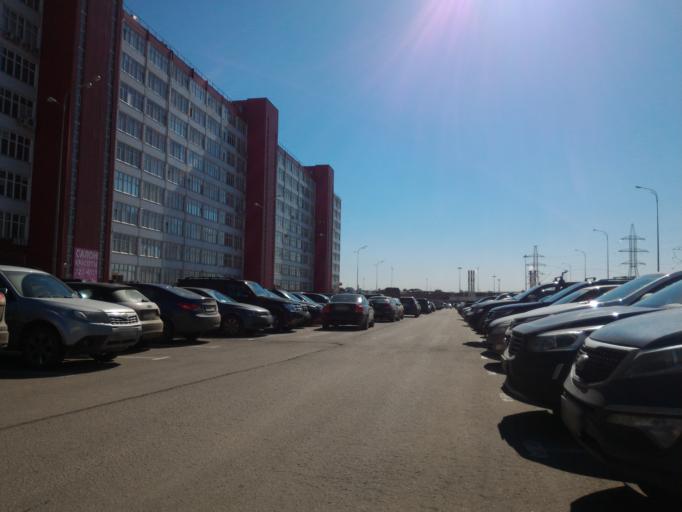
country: RU
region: Moskovskaya
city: Mosrentgen
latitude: 55.6356
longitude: 37.4355
